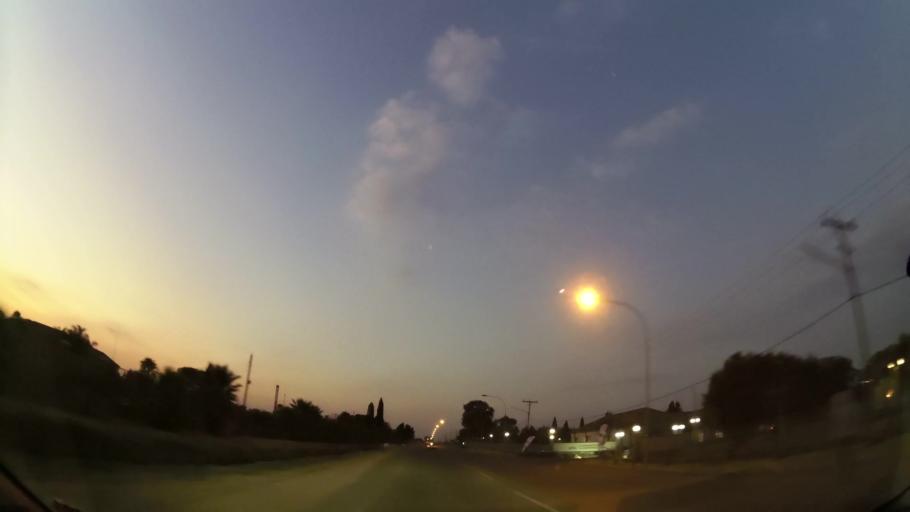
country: ZA
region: Gauteng
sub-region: Ekurhuleni Metropolitan Municipality
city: Benoni
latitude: -26.1076
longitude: 28.3192
